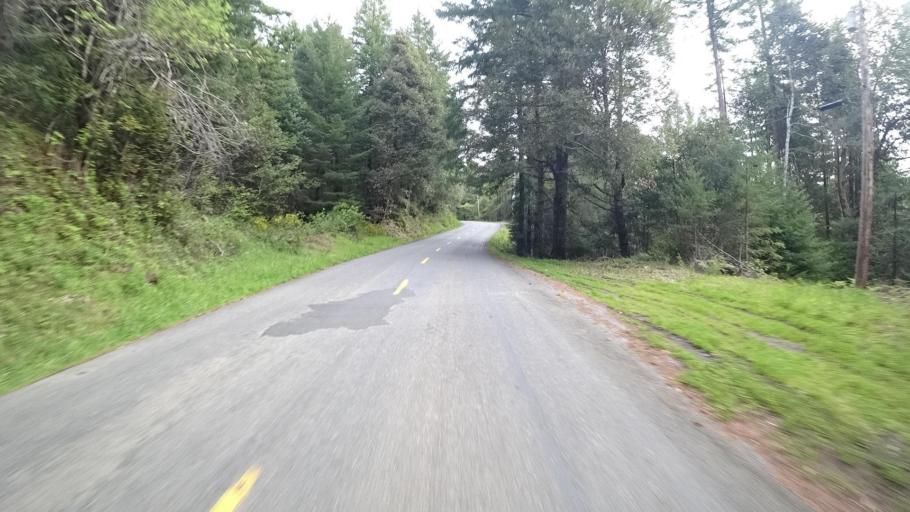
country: US
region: California
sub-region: Humboldt County
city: Redway
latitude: 40.2886
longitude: -123.8361
